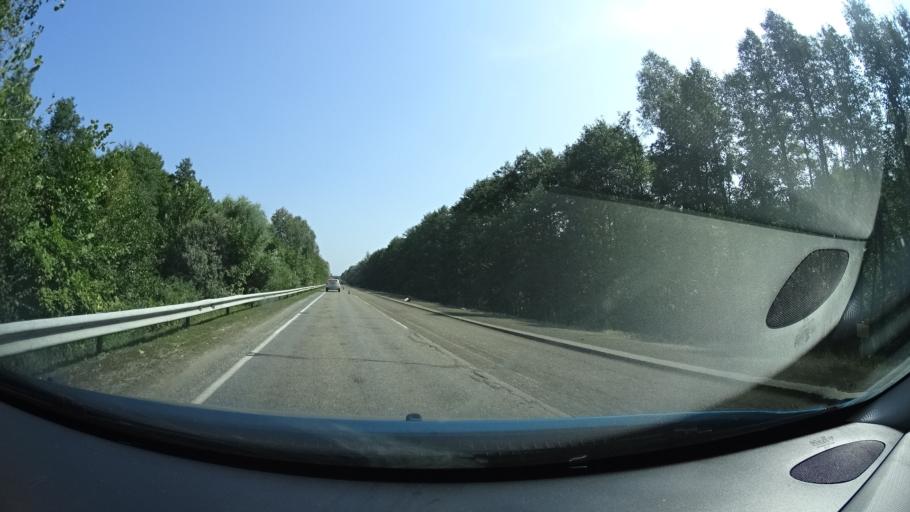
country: RU
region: Bashkortostan
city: Ulukulevo
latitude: 54.4543
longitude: 56.5020
